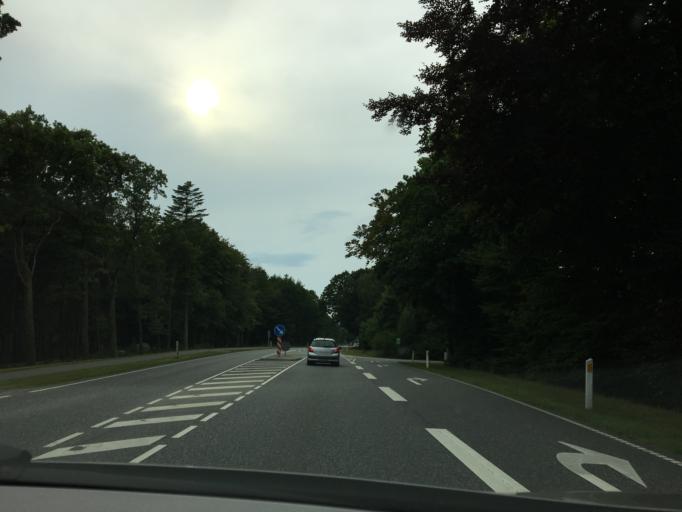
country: DK
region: Central Jutland
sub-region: Ringkobing-Skjern Kommune
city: Ringkobing
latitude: 56.0844
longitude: 8.3188
